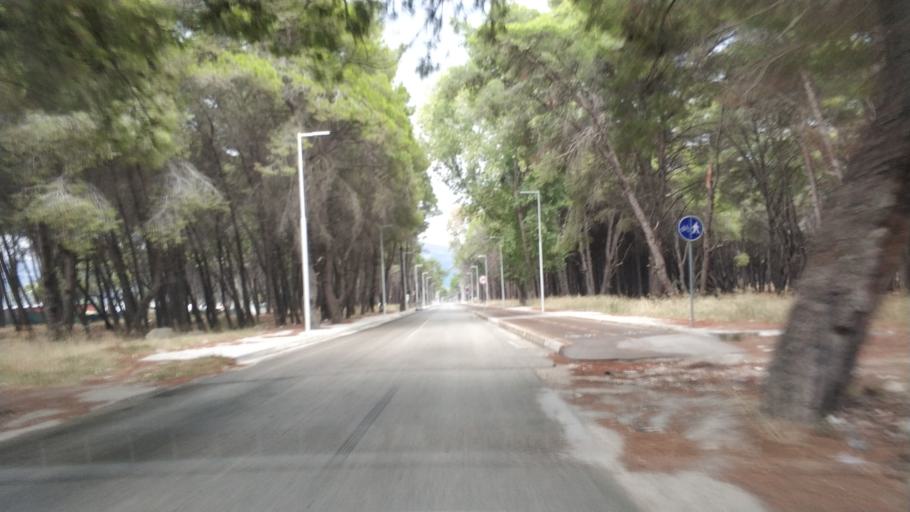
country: AL
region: Vlore
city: Vlore
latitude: 40.4675
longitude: 19.4611
